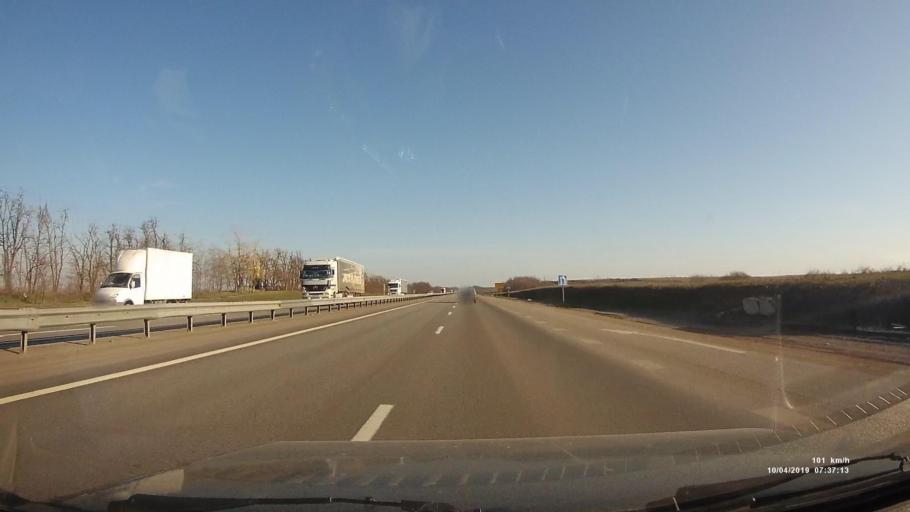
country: RU
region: Rostov
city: Likhoy
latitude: 48.0699
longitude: 40.2592
